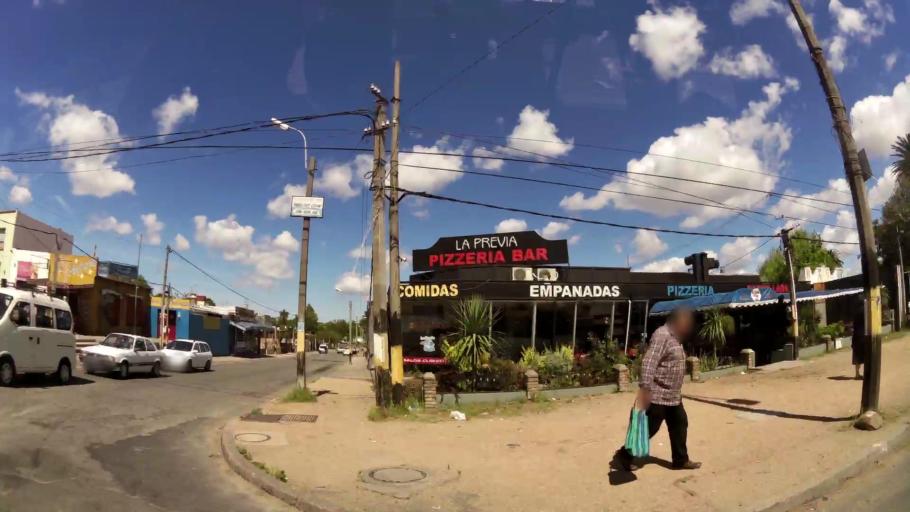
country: UY
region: Montevideo
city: Montevideo
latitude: -34.8461
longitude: -56.1352
